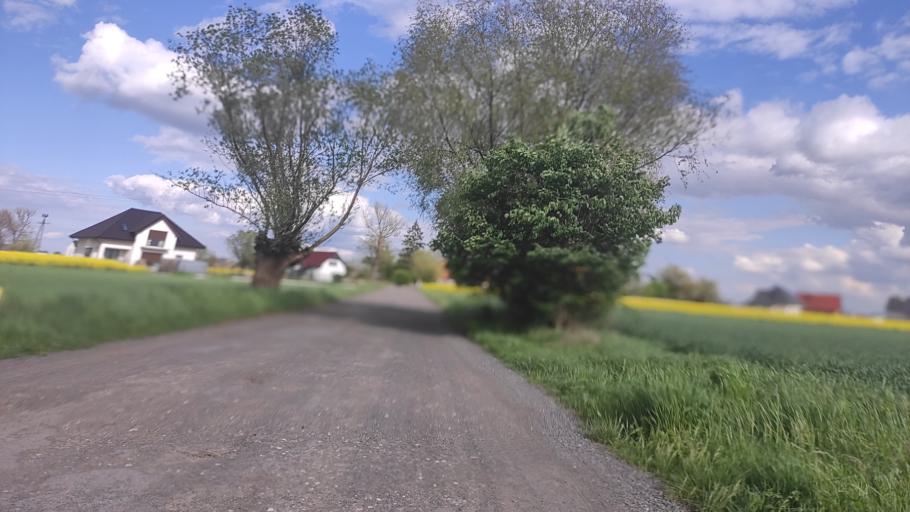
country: PL
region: Greater Poland Voivodeship
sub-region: Powiat poznanski
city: Kleszczewo
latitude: 52.3861
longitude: 17.1422
